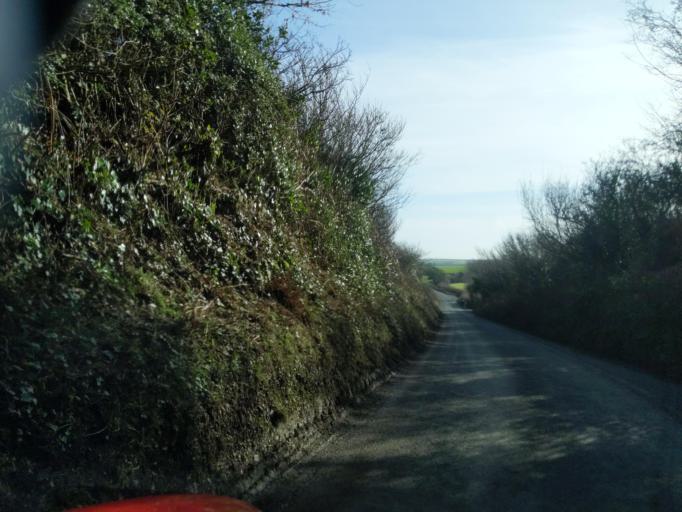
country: GB
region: England
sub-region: Devon
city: Kingsbridge
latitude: 50.3456
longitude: -3.7266
